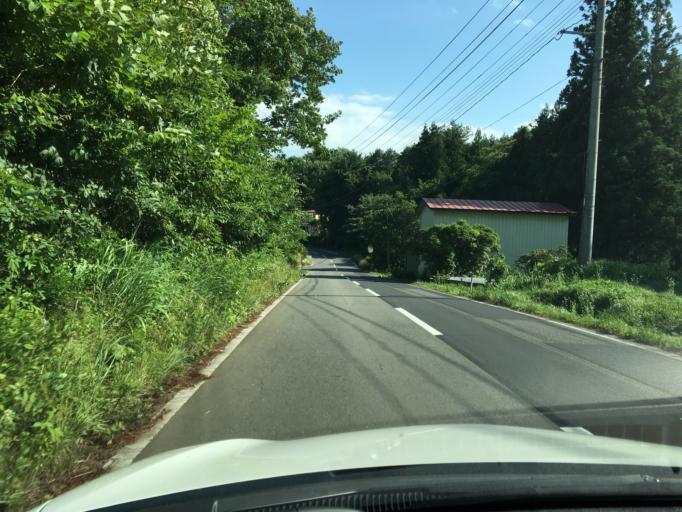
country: JP
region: Fukushima
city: Ishikawa
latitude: 37.2278
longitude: 140.5449
